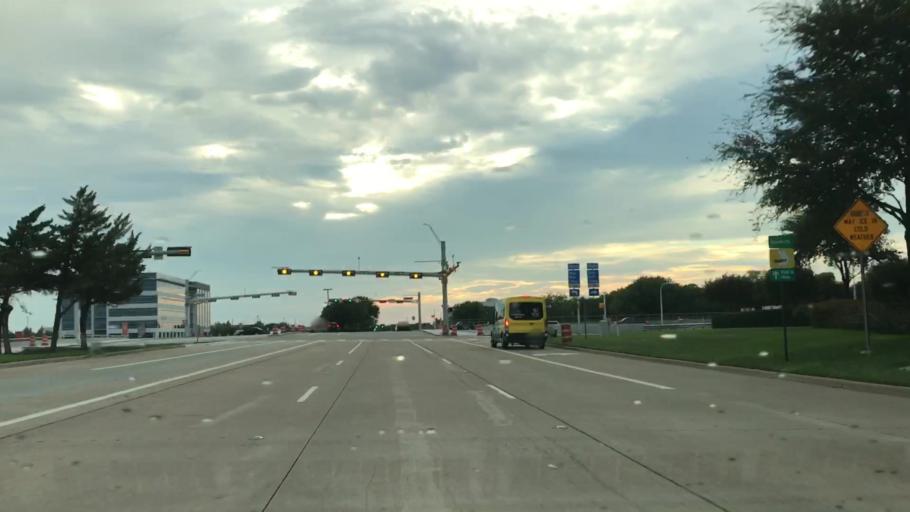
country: US
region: Texas
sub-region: Denton County
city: The Colony
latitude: 33.0721
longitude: -96.8234
